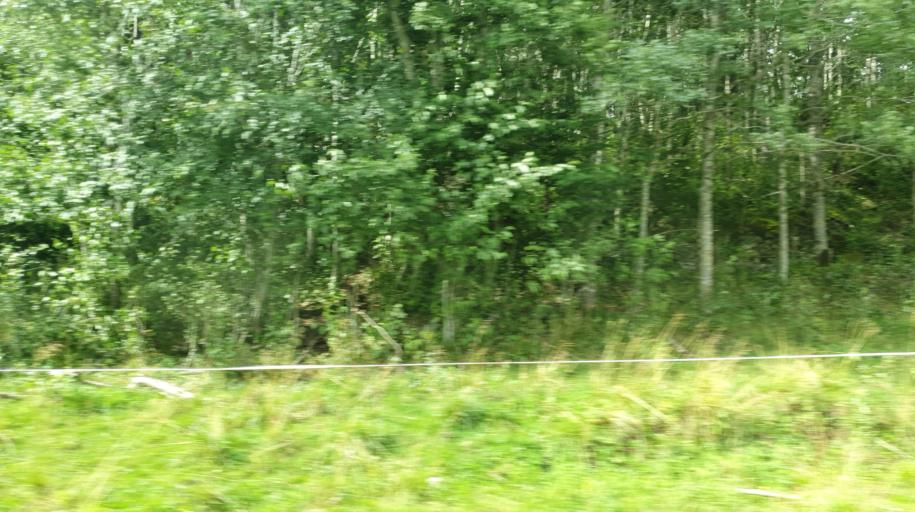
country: NO
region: Nord-Trondelag
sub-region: Levanger
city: Skogn
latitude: 63.5980
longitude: 11.2705
